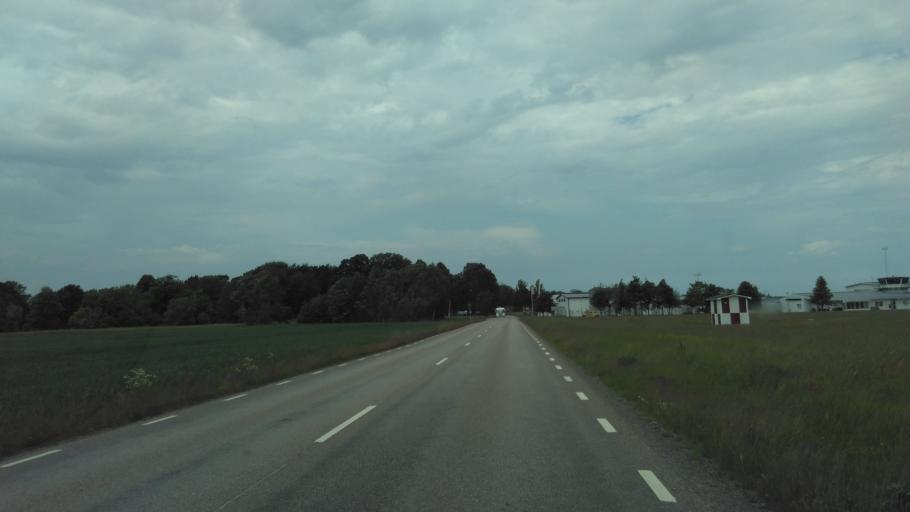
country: SE
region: Vaestra Goetaland
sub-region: Lidkopings Kommun
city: Lidkoping
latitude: 58.4598
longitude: 13.1549
